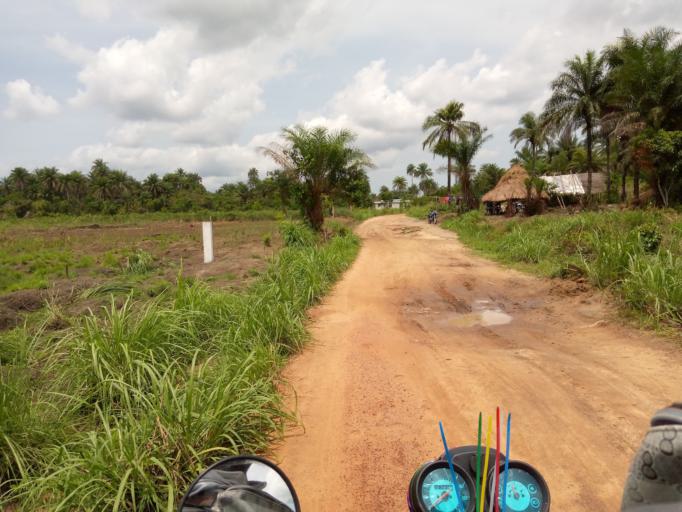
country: SL
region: Western Area
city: Waterloo
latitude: 8.3214
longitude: -12.9409
